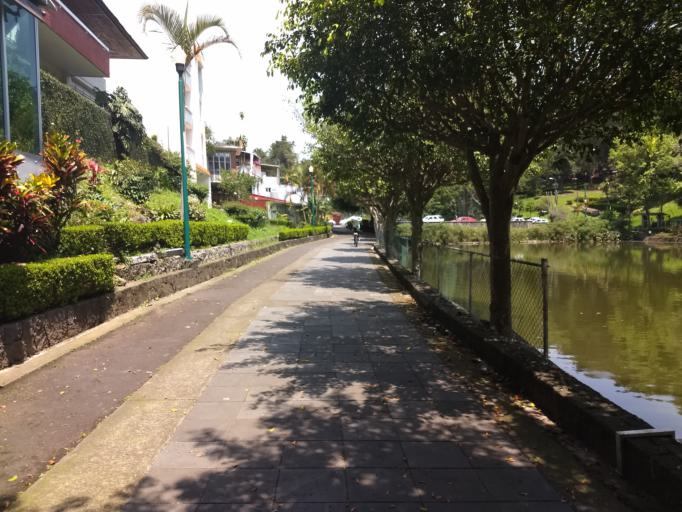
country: MX
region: Veracruz
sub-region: Xalapa
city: Xalapa de Enriquez
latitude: 19.5167
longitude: -96.9203
